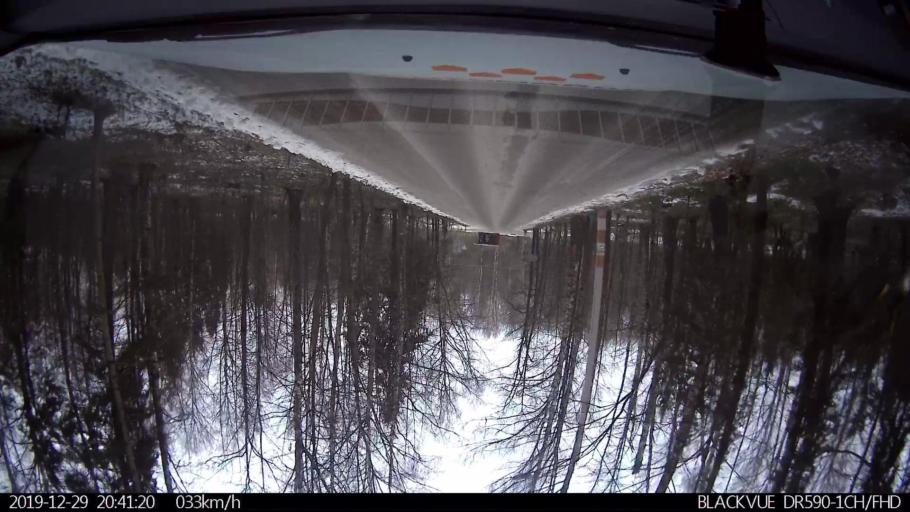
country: RU
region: Nizjnij Novgorod
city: Afonino
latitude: 56.1874
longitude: 44.0386
